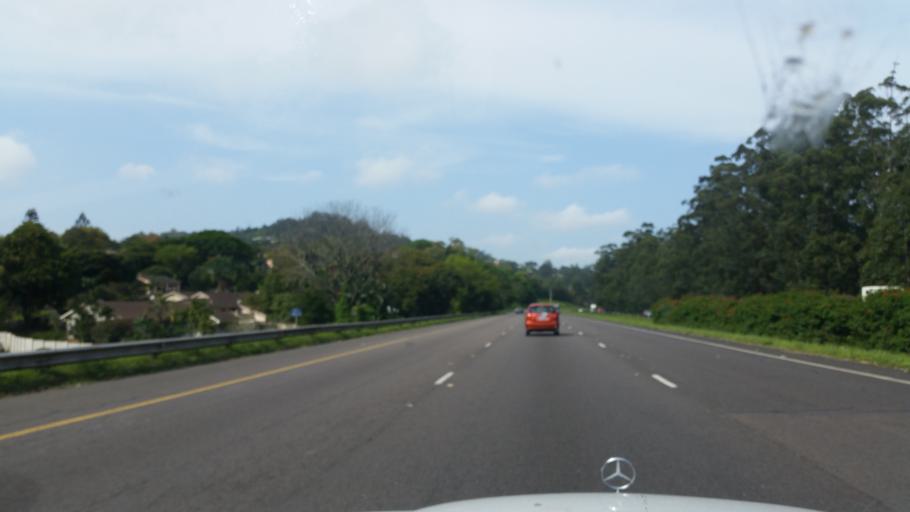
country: ZA
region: KwaZulu-Natal
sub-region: eThekwini Metropolitan Municipality
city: Berea
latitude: -29.8360
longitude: 30.8777
